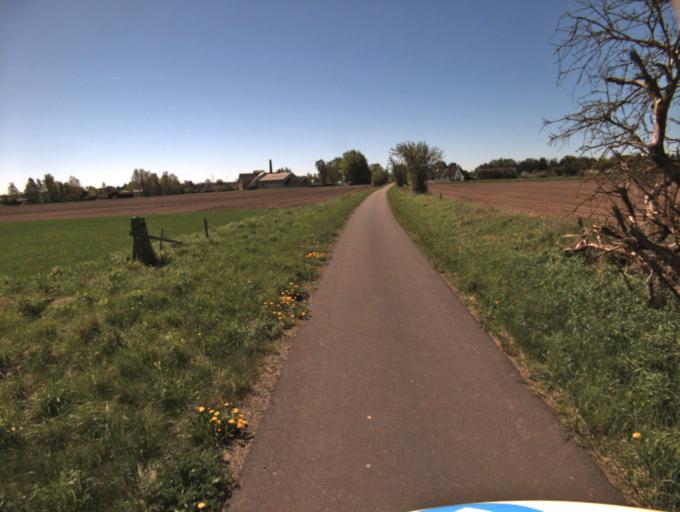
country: SE
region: Skane
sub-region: Kristianstads Kommun
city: Norra Asum
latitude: 55.9531
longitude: 14.1560
